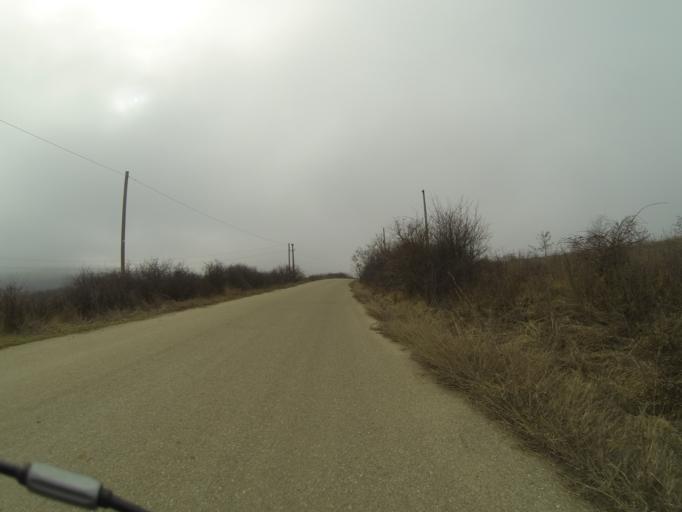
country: RO
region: Mehedinti
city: Dumbrava de Sus
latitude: 44.4900
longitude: 23.0819
